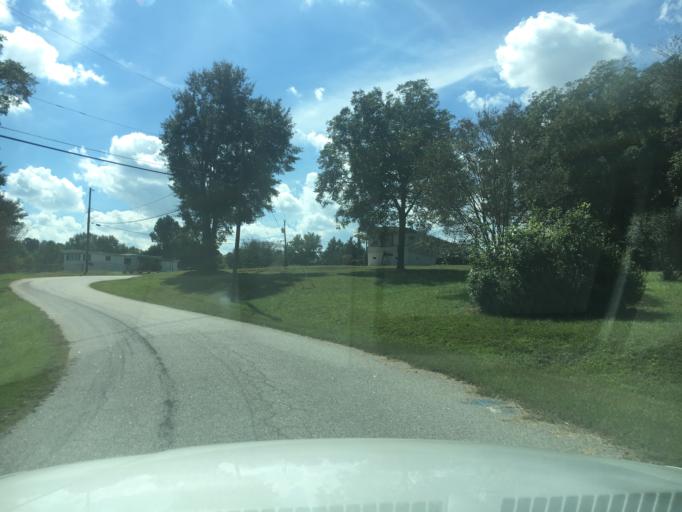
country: US
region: South Carolina
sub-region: Spartanburg County
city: Duncan
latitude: 34.9471
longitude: -82.1543
